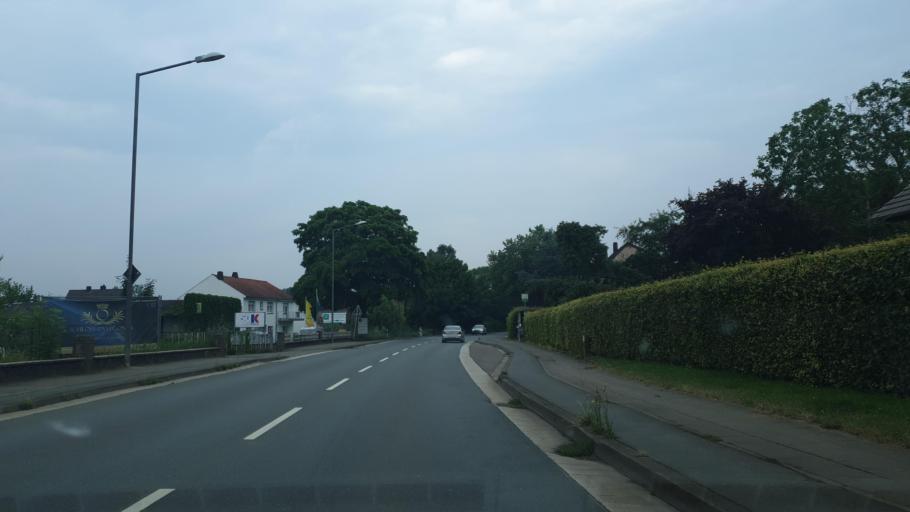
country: DE
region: North Rhine-Westphalia
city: Bad Oeynhausen
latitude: 52.2279
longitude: 8.7979
